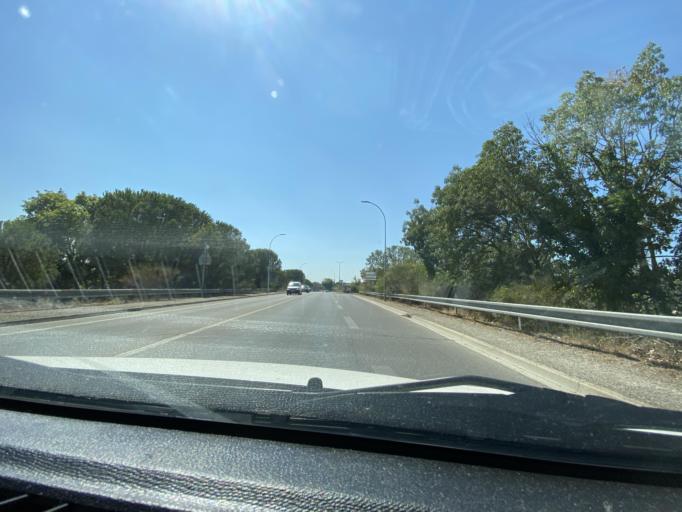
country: FR
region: Provence-Alpes-Cote d'Azur
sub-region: Departement des Bouches-du-Rhone
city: Salon-de-Provence
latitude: 43.6294
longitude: 5.1181
